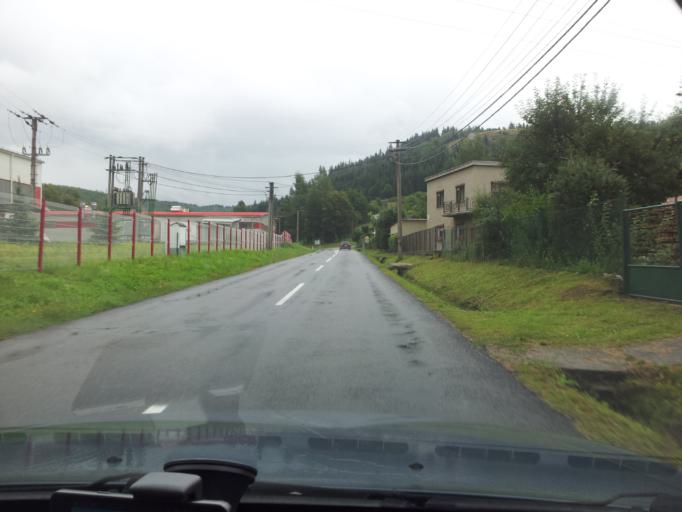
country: SK
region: Banskobystricky
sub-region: Okres Banska Bystrica
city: Brezno
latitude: 48.8165
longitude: 19.5599
